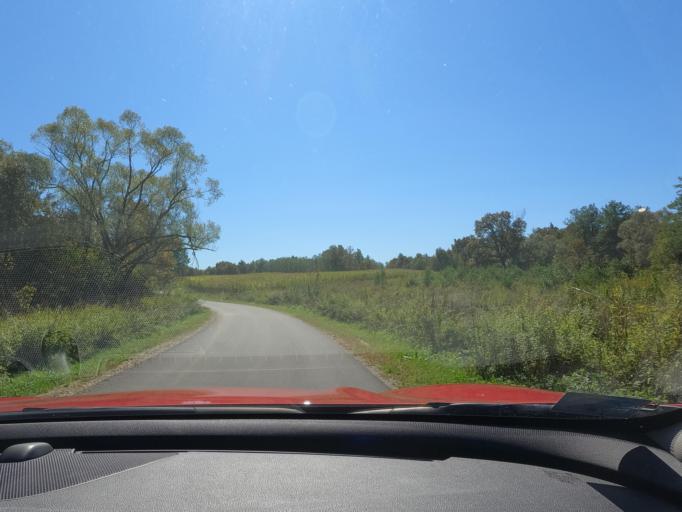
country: HR
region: Sisacko-Moslavacka
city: Petrinja
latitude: 45.3676
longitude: 16.2364
